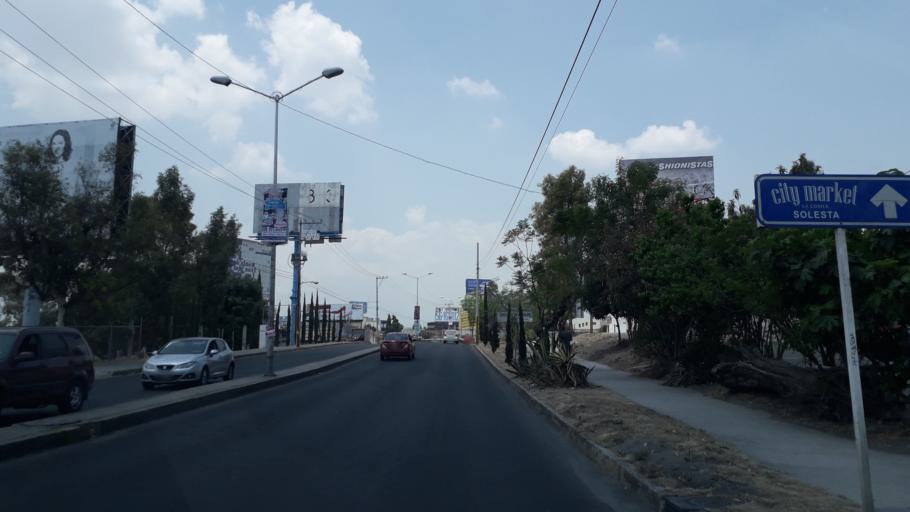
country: MX
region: Puebla
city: Puebla
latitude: 19.0261
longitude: -98.2248
